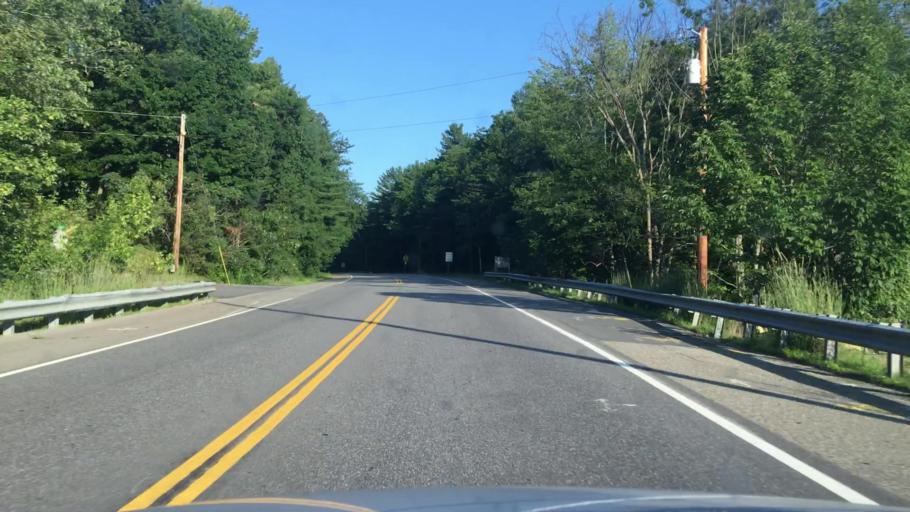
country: US
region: Maine
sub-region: Androscoggin County
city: Lisbon Falls
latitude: 44.0073
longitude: -70.0809
